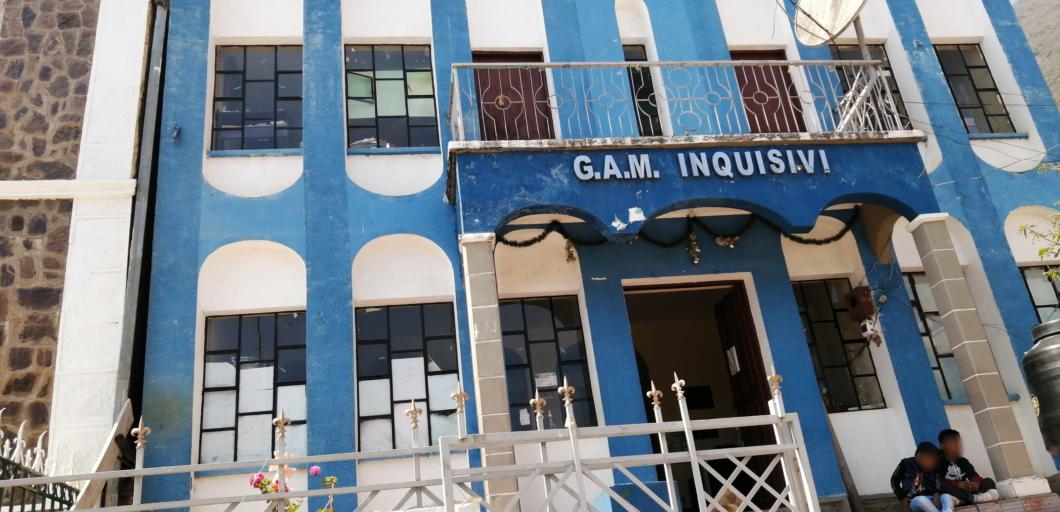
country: BO
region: La Paz
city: Quime
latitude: -16.9076
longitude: -67.1378
